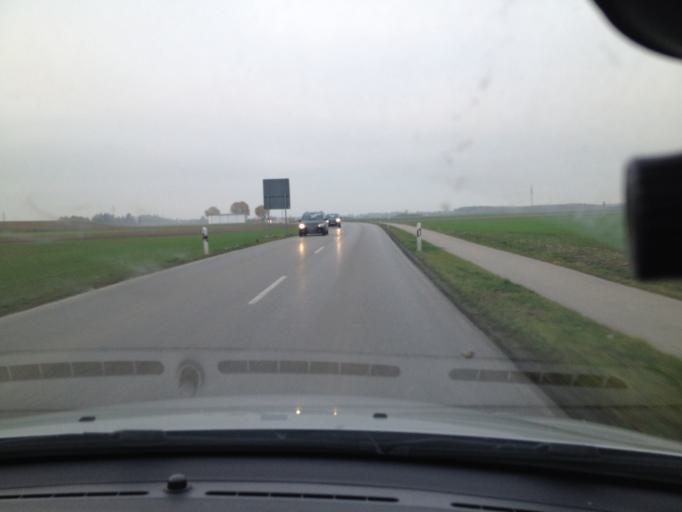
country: DE
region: Bavaria
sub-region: Swabia
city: Graben
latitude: 48.2003
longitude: 10.8268
